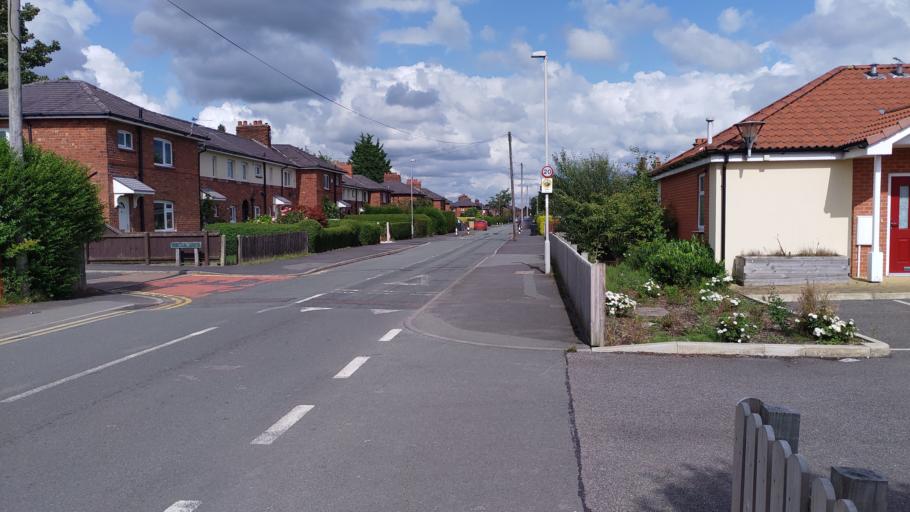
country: GB
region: England
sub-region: Lancashire
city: Preston
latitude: 53.7747
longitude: -2.6807
